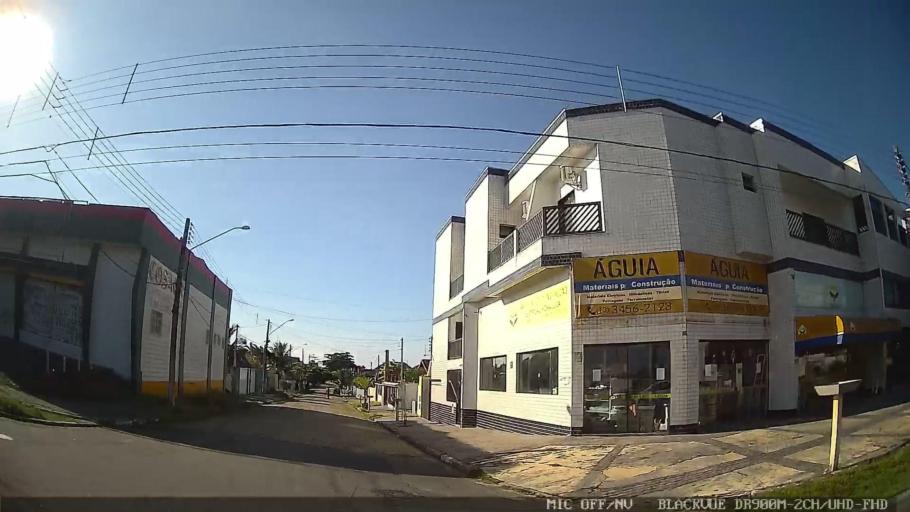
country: BR
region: Sao Paulo
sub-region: Peruibe
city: Peruibe
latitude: -24.2900
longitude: -46.9613
